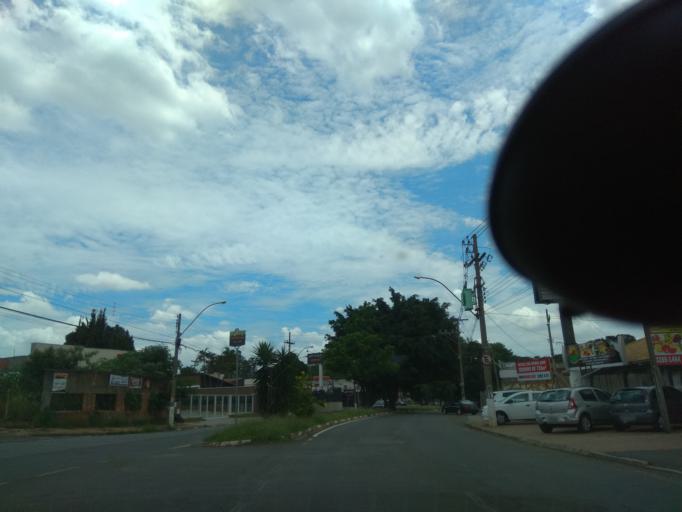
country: BR
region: Sao Paulo
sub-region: Campinas
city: Campinas
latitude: -22.8335
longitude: -47.0777
